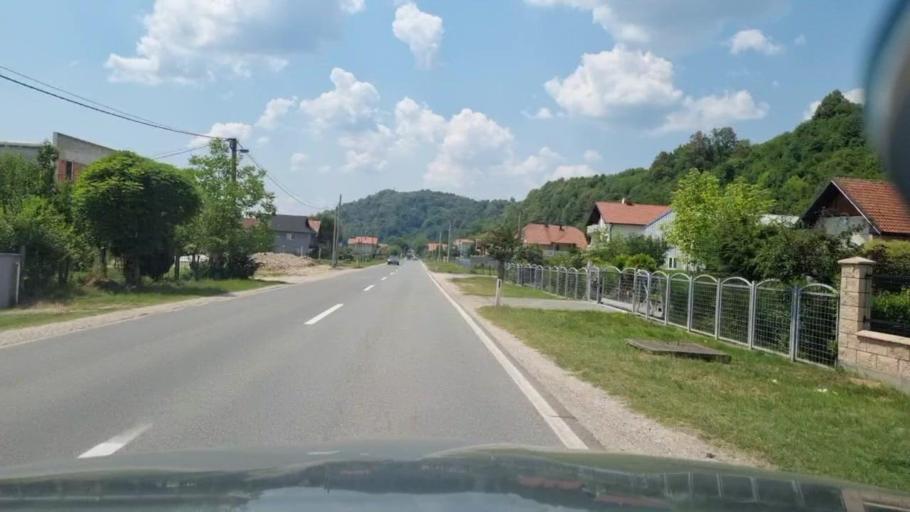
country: BA
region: Federation of Bosnia and Herzegovina
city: Gornja Tuzla
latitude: 44.5308
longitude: 18.7584
